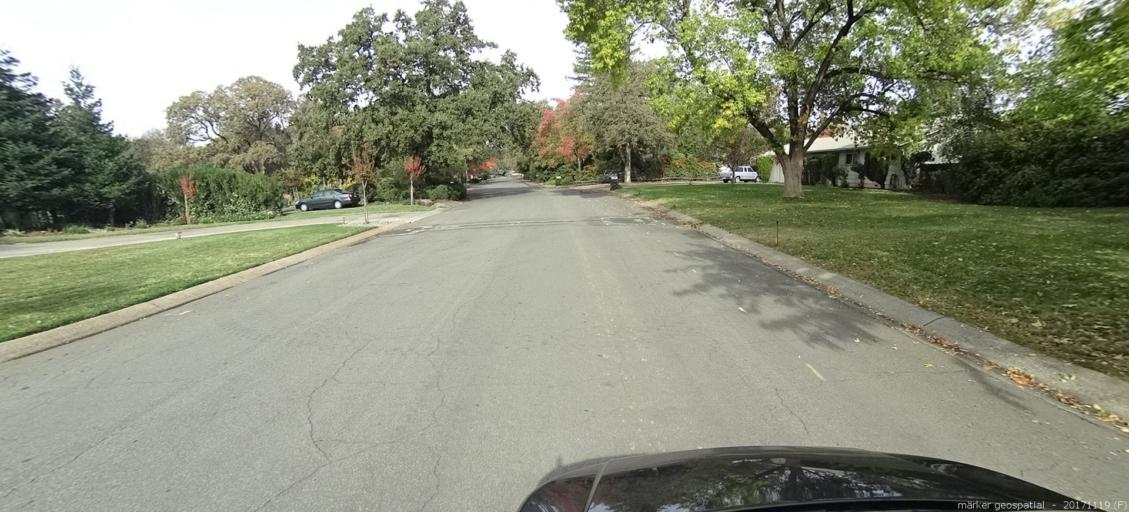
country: US
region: California
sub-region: Shasta County
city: Anderson
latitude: 40.4920
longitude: -122.3096
